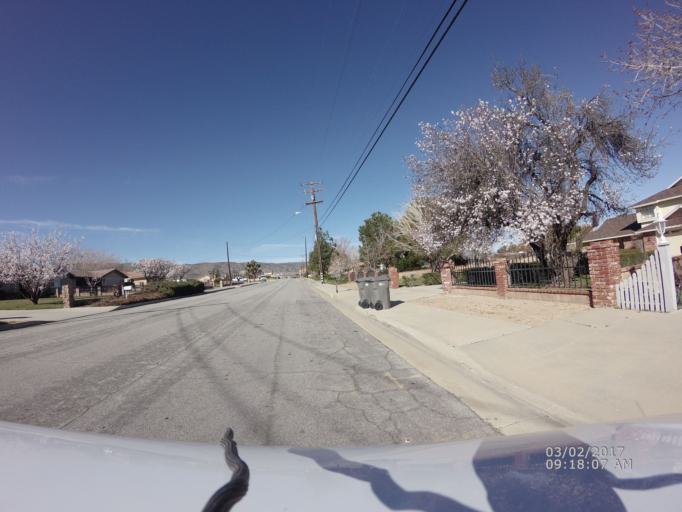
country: US
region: California
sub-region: Los Angeles County
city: Quartz Hill
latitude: 34.6345
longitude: -118.2166
